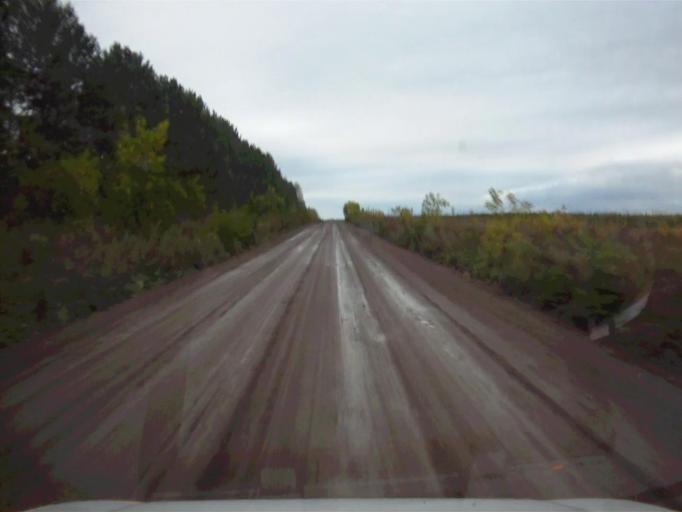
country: RU
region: Sverdlovsk
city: Mikhaylovsk
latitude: 56.1610
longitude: 59.2472
